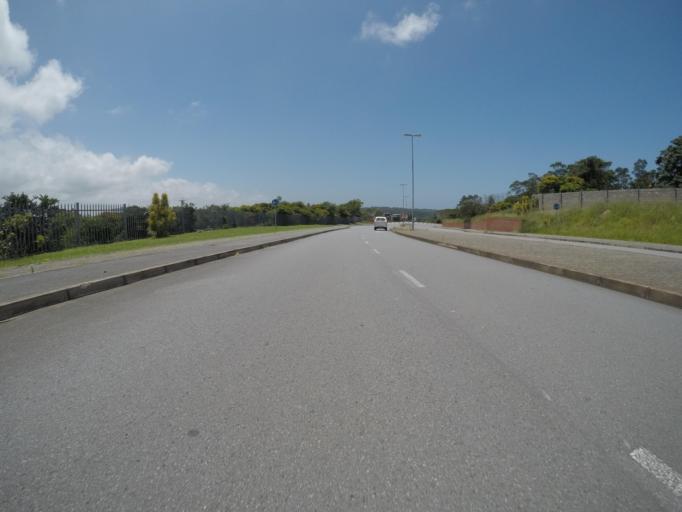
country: ZA
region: Eastern Cape
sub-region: Buffalo City Metropolitan Municipality
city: East London
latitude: -32.9499
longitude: 27.9385
